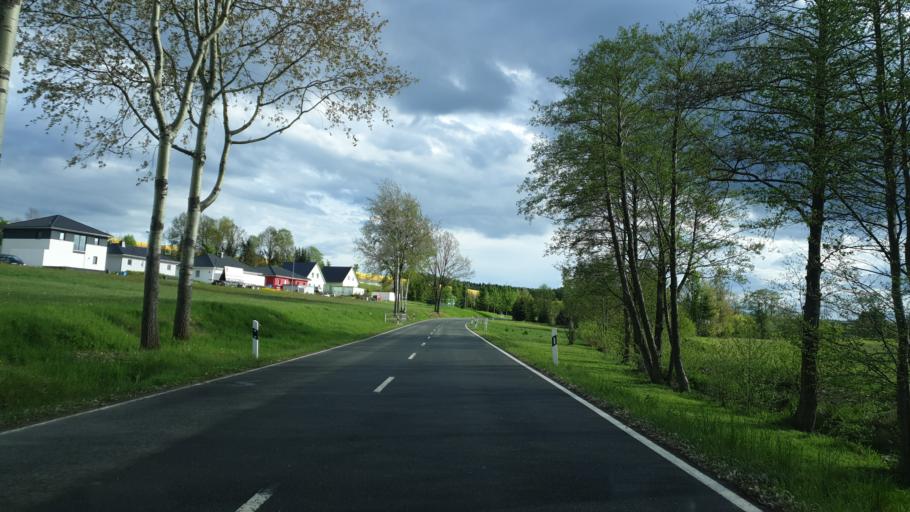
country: DE
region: Saxony
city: Oelsnitz
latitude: 50.6987
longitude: 12.7298
